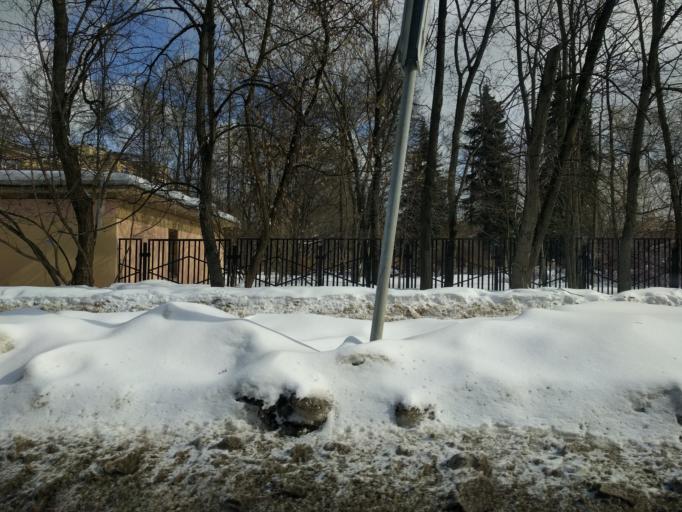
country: RU
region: Moscow
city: Metrogorodok
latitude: 55.8014
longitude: 37.7749
